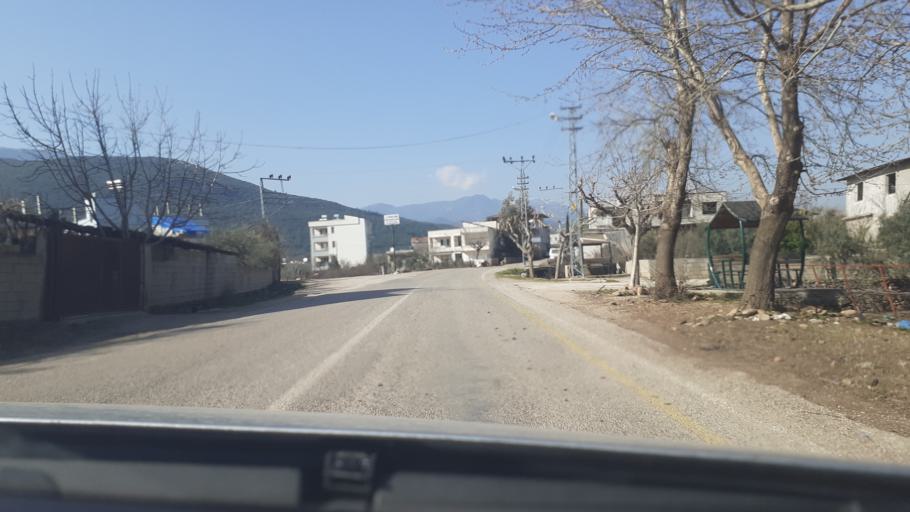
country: TR
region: Hatay
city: Aktepe
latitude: 36.7105
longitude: 36.4862
